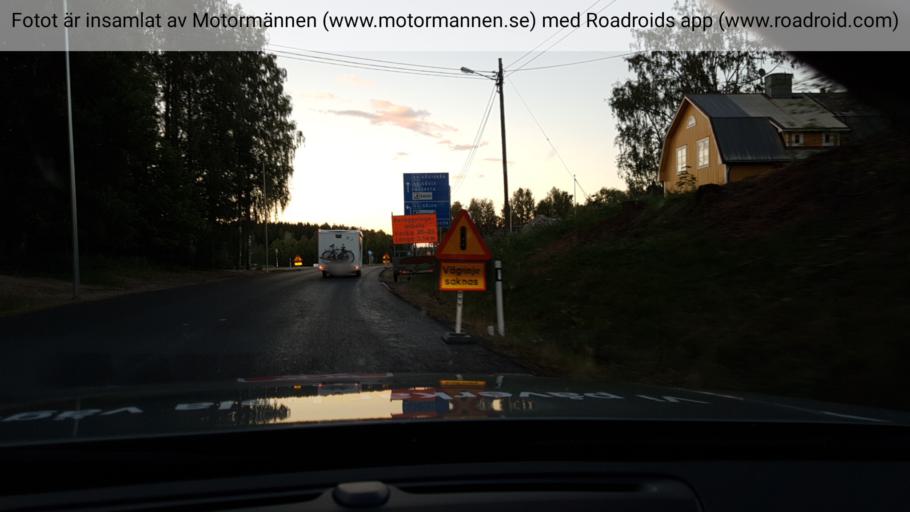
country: SE
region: Vaestmanland
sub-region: Fagersta Kommun
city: Fagersta
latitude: 59.9632
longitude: 15.7655
